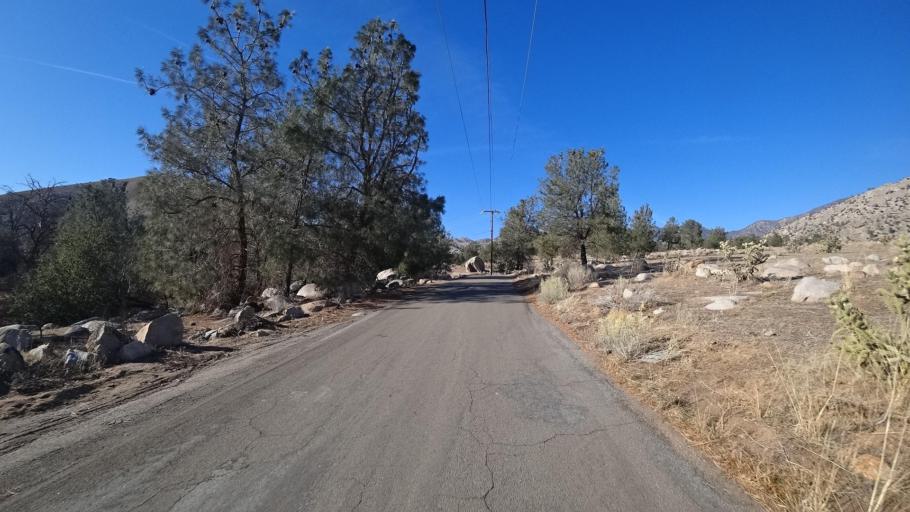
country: US
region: California
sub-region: Kern County
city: Weldon
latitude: 35.6980
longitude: -118.2970
